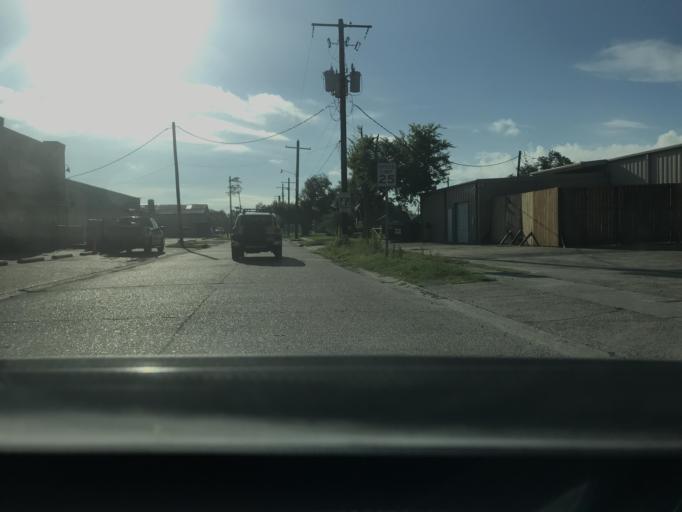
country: US
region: Louisiana
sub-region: Calcasieu Parish
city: Lake Charles
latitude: 30.2069
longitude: -93.2185
